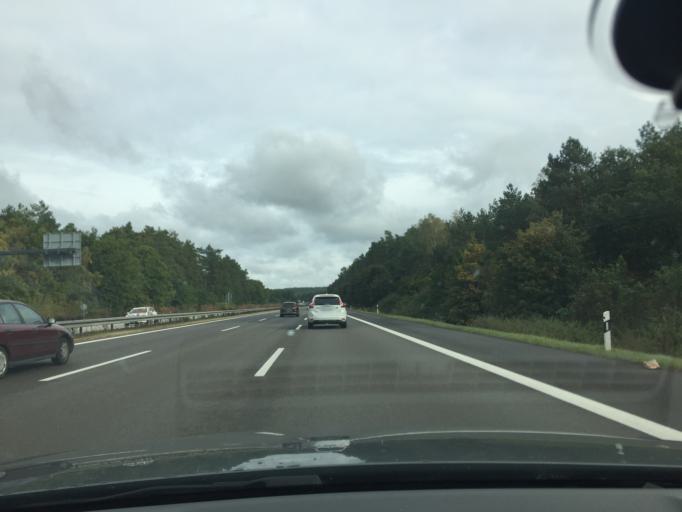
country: DE
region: Brandenburg
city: Grunheide
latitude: 52.4321
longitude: 13.7924
